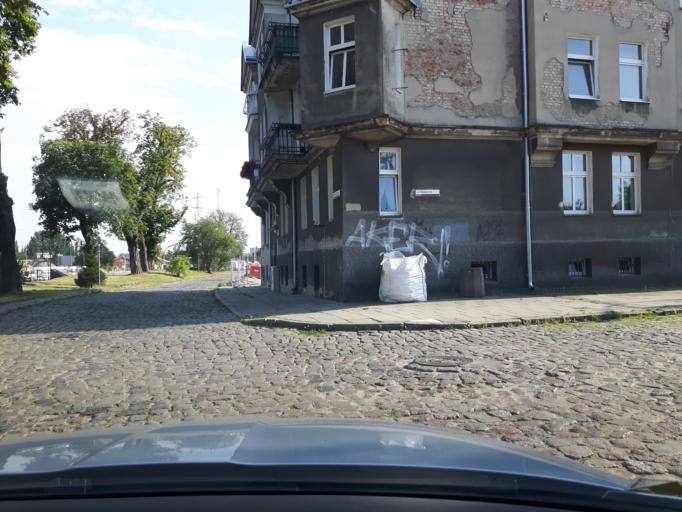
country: PL
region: Pomeranian Voivodeship
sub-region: Gdansk
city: Gdansk
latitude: 54.3574
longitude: 18.6655
